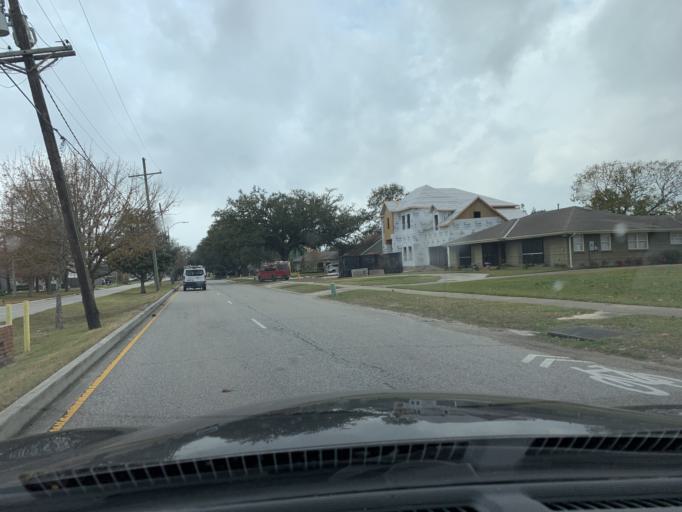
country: US
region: Louisiana
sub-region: Jefferson Parish
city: Metairie
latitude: 30.0190
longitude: -90.0999
